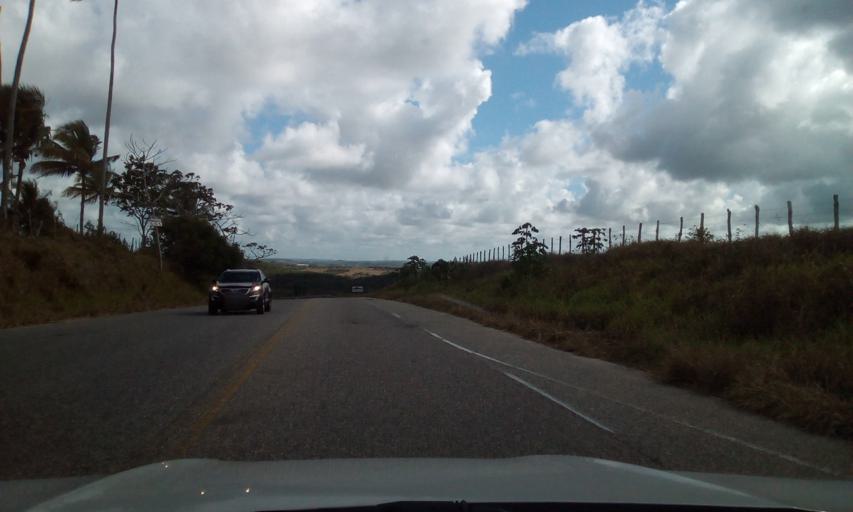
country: BR
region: Sergipe
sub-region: Estancia
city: Estancia
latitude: -11.3139
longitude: -37.4526
